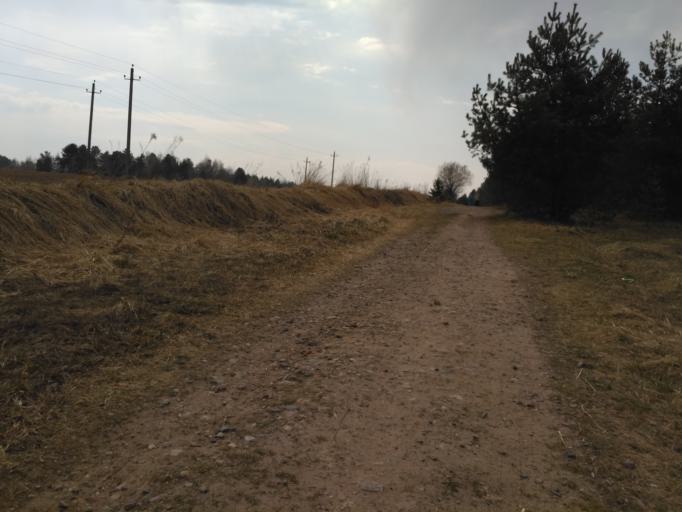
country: BY
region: Minsk
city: Zamostochcha
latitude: 53.8825
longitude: 27.9113
